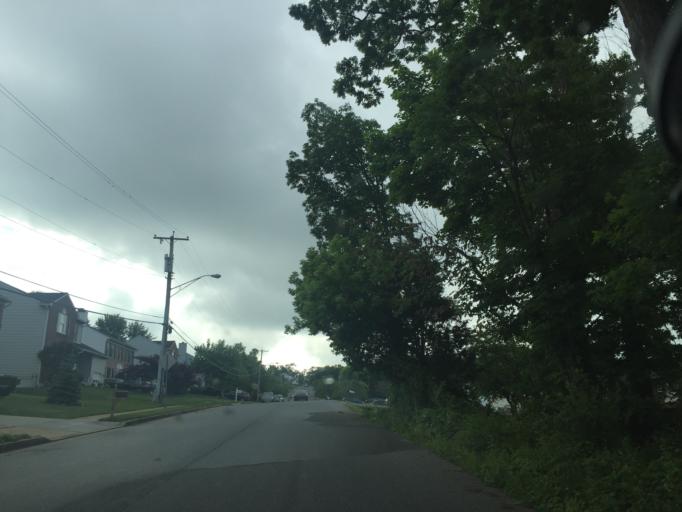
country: US
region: Maryland
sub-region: Baltimore County
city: Perry Hall
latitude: 39.3831
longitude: -76.4834
